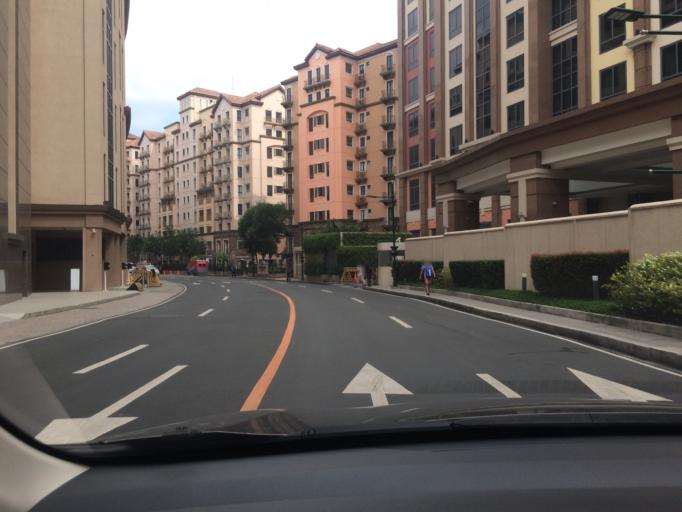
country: PH
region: Metro Manila
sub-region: Makati City
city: Makati City
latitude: 14.5209
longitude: 121.0179
